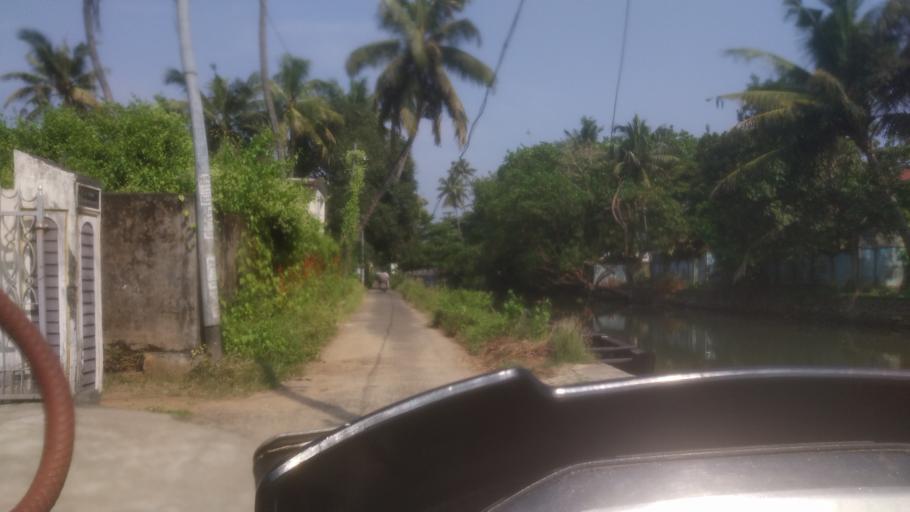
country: IN
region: Kerala
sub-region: Ernakulam
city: Elur
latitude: 10.0485
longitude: 76.2181
